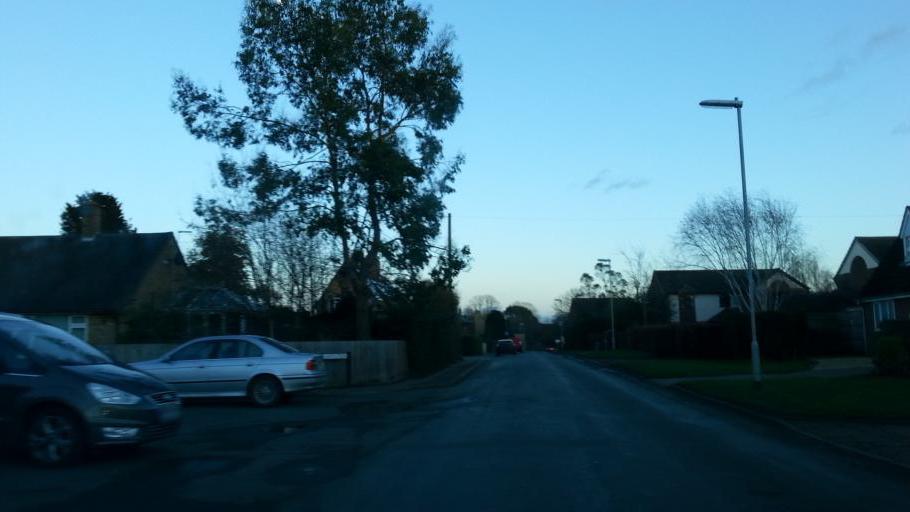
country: GB
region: England
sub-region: Cambridgeshire
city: Needingworth
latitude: 52.2976
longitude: -0.0405
